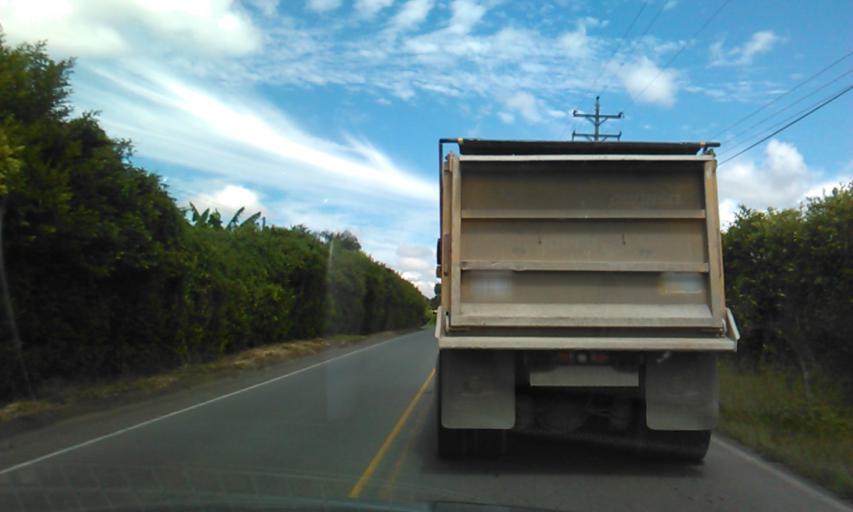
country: CO
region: Quindio
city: Cordoba
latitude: 4.4357
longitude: -75.7168
